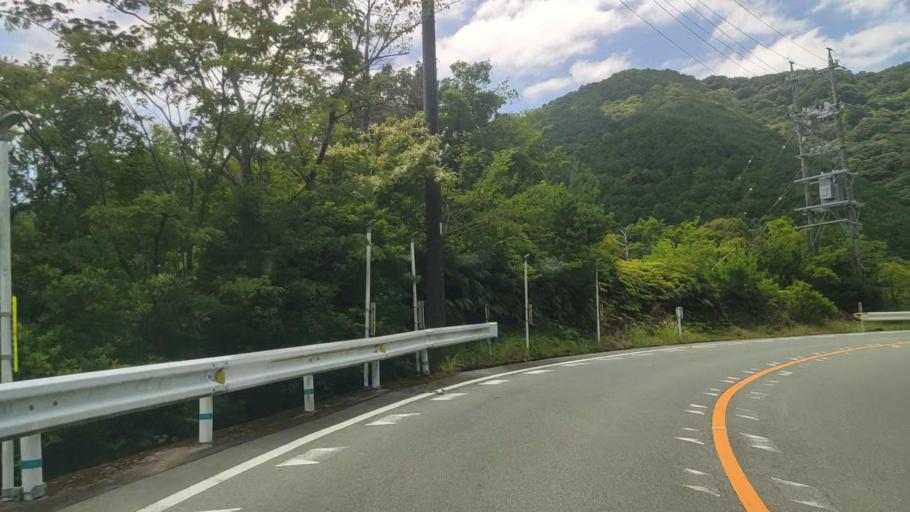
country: JP
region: Mie
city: Owase
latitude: 34.2171
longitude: 136.3767
